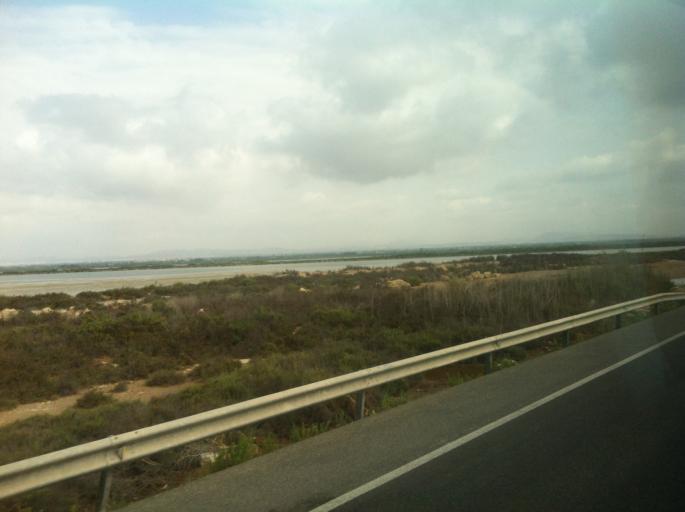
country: ES
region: Valencia
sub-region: Provincia de Alicante
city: Santa Pola
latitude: 38.1798
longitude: -0.6187
